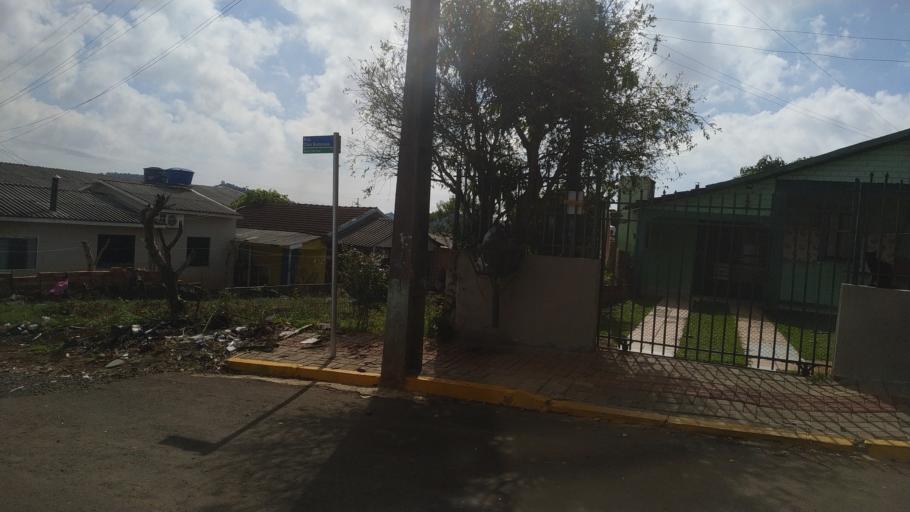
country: BR
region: Santa Catarina
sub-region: Chapeco
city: Chapeco
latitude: -27.0676
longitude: -52.6043
